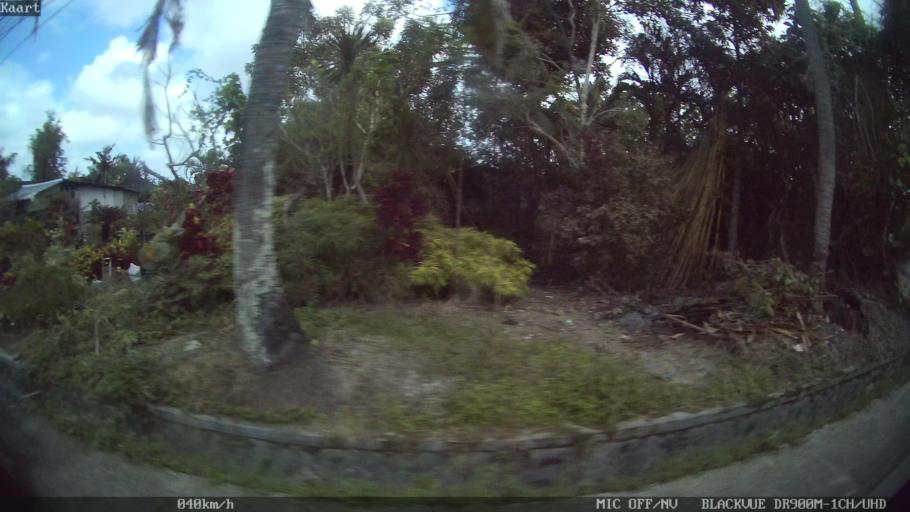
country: ID
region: Bali
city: Banjar Pasekan
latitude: -8.5812
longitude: 115.2951
